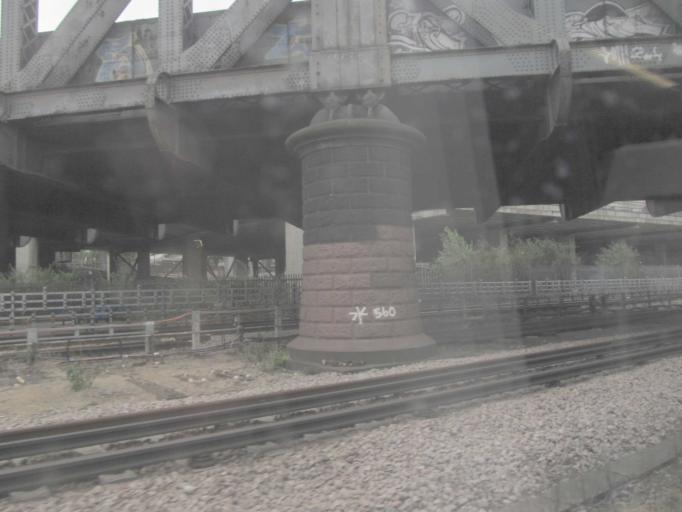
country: GB
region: England
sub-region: Greater London
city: Bayswater
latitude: 51.5188
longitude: -0.1846
